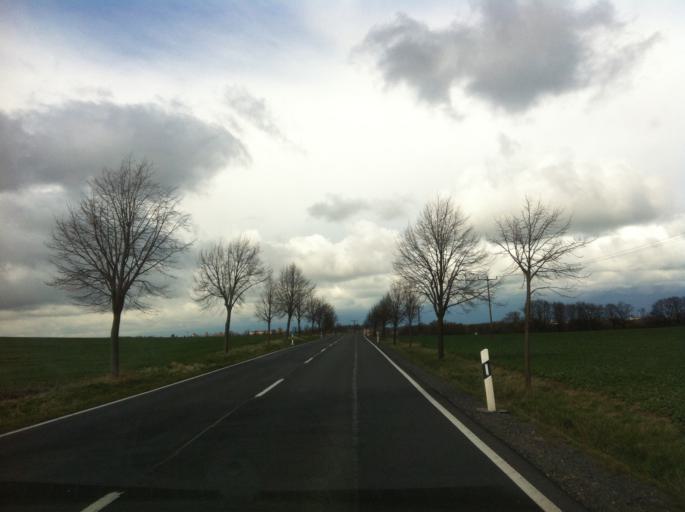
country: DE
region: Saxony
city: Bennewitz
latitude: 51.3312
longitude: 12.7360
